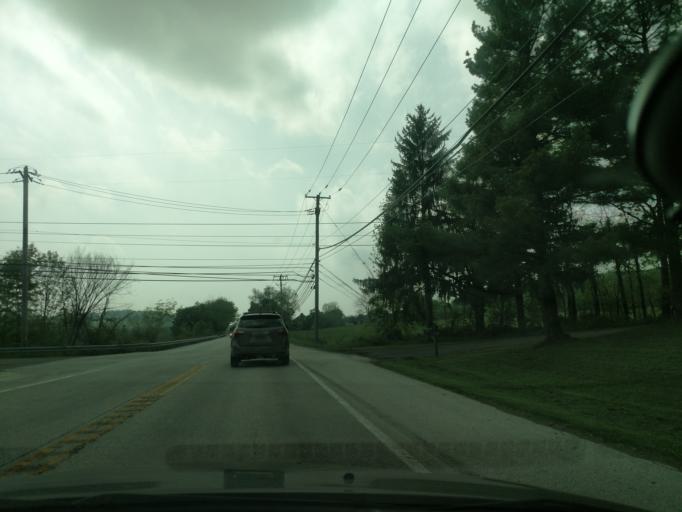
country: US
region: Pennsylvania
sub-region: Chester County
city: South Pottstown
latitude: 40.1741
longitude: -75.6775
